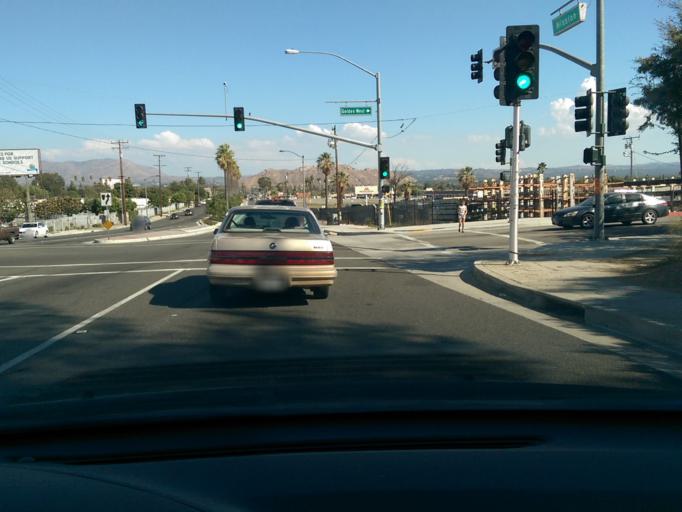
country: US
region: California
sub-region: Riverside County
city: Sunnyslope
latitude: 34.0084
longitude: -117.4298
